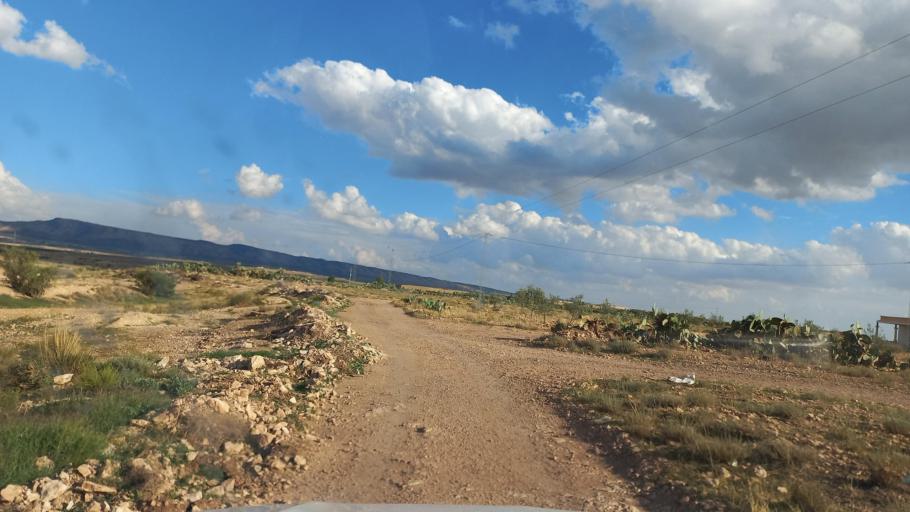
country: TN
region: Al Qasrayn
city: Sbiba
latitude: 35.3831
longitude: 9.0700
